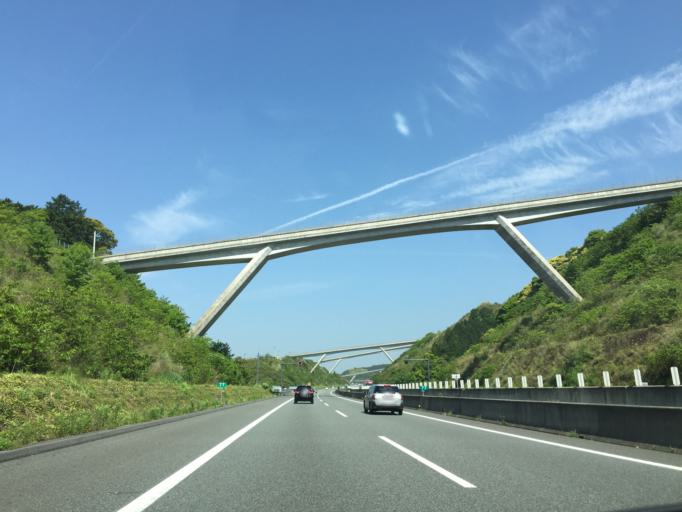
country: JP
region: Shizuoka
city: Fuji
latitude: 35.1650
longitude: 138.7563
